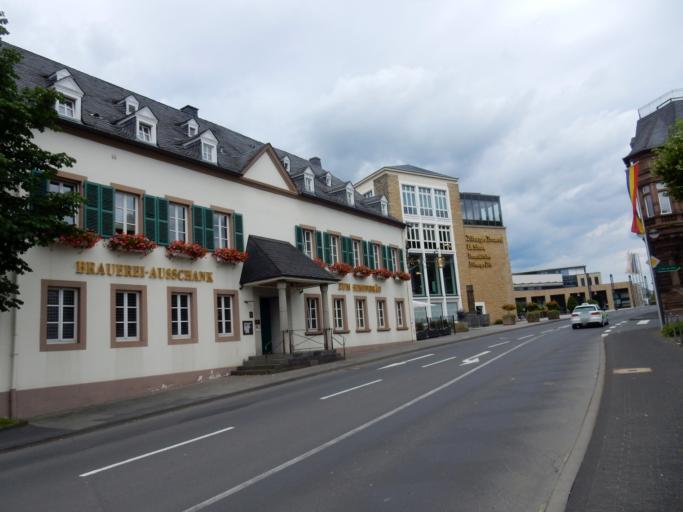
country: DE
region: Rheinland-Pfalz
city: Bitburg
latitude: 49.9736
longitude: 6.5224
